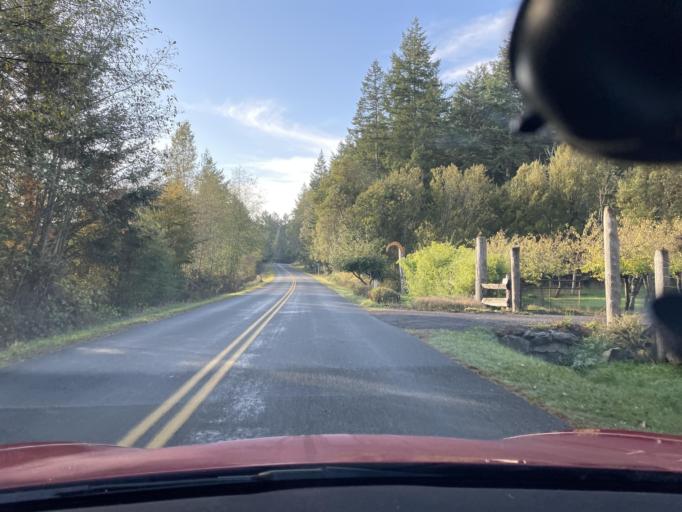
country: US
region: Washington
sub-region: San Juan County
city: Friday Harbor
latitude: 48.5605
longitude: -123.1646
